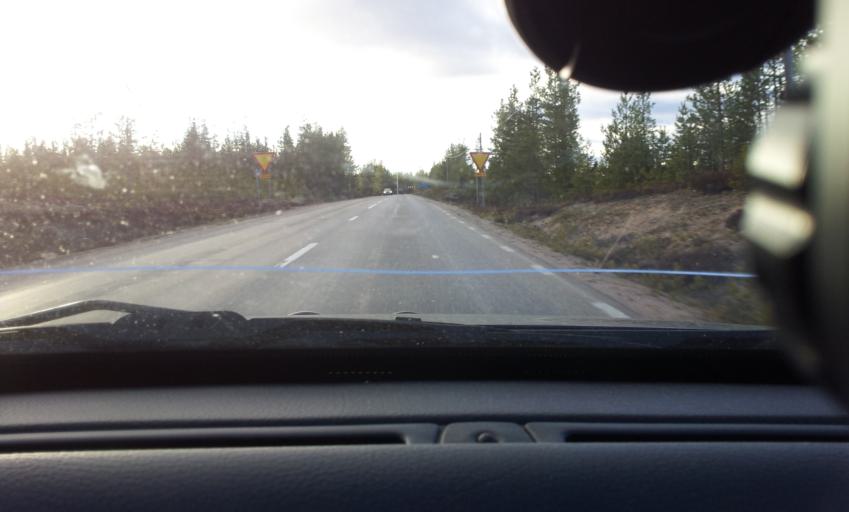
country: SE
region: Jaemtland
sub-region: Harjedalens Kommun
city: Sveg
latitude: 62.1275
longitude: 14.9791
